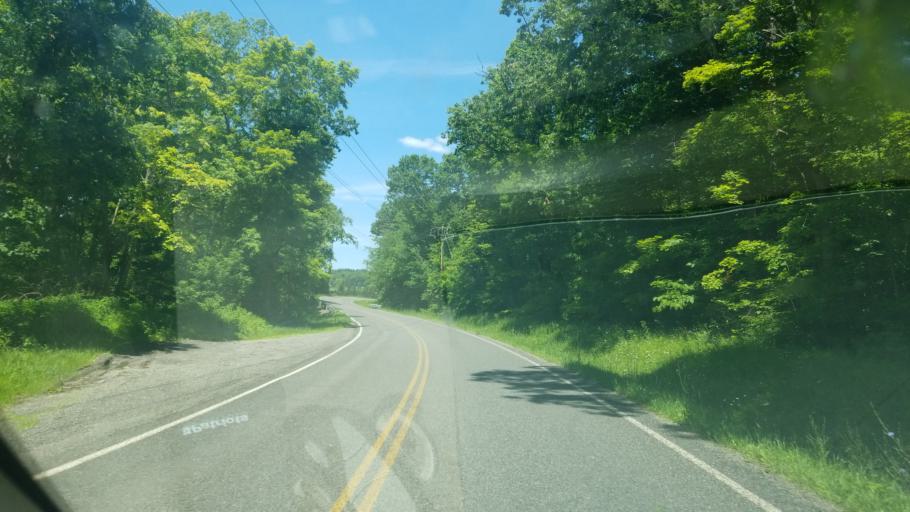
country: US
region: Ohio
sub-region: Columbiana County
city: Glenmoor
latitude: 40.7404
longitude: -80.6430
